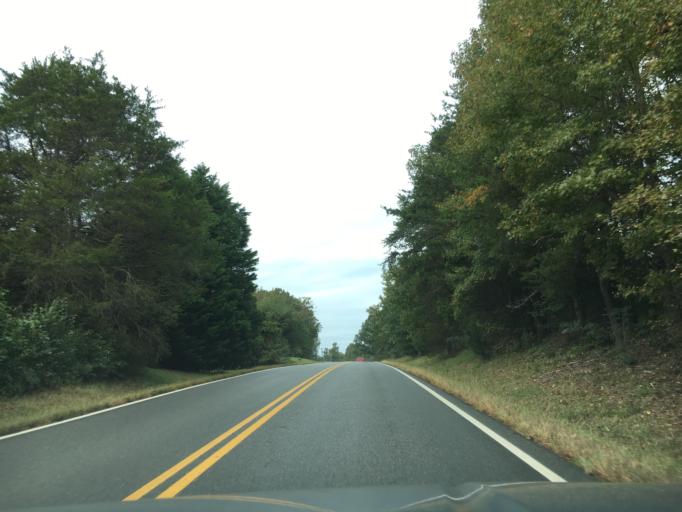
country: US
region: Virginia
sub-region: Goochland County
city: Goochland
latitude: 37.7386
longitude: -77.8435
